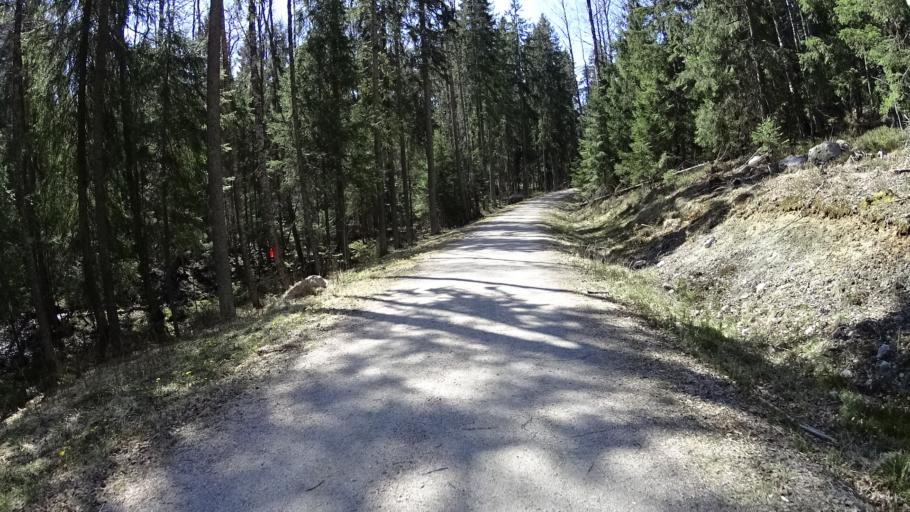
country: FI
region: Uusimaa
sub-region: Helsinki
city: Espoo
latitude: 60.2073
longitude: 24.6214
